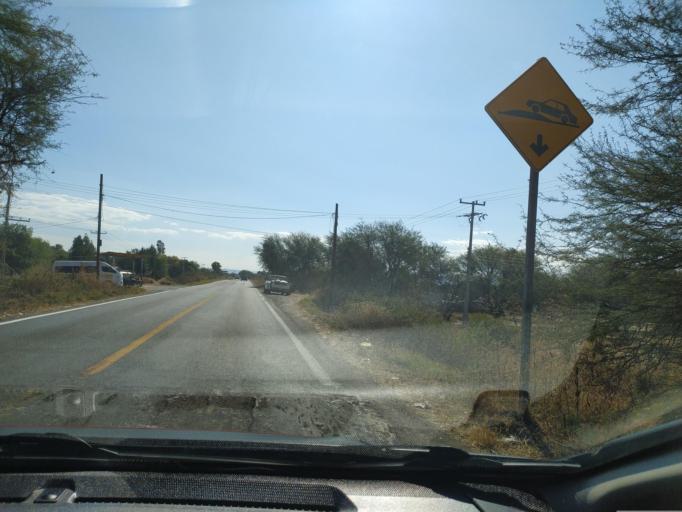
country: MX
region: Guanajuato
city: Ciudad Manuel Doblado
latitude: 20.8145
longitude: -101.9030
